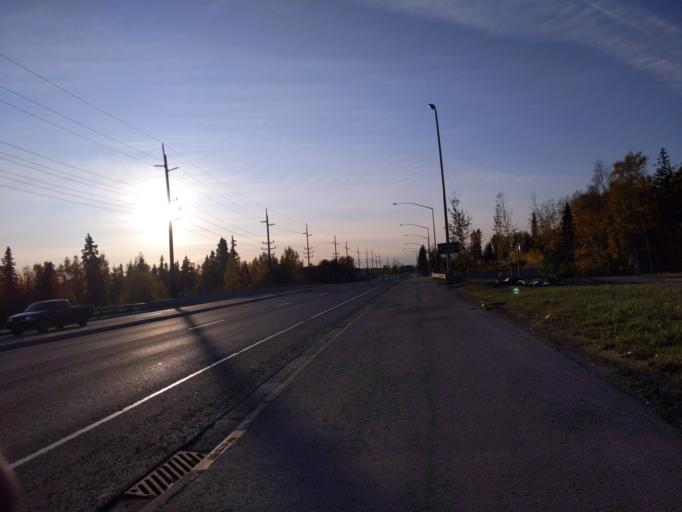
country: US
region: Alaska
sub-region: Anchorage Municipality
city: Anchorage
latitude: 61.1665
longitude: -149.8725
